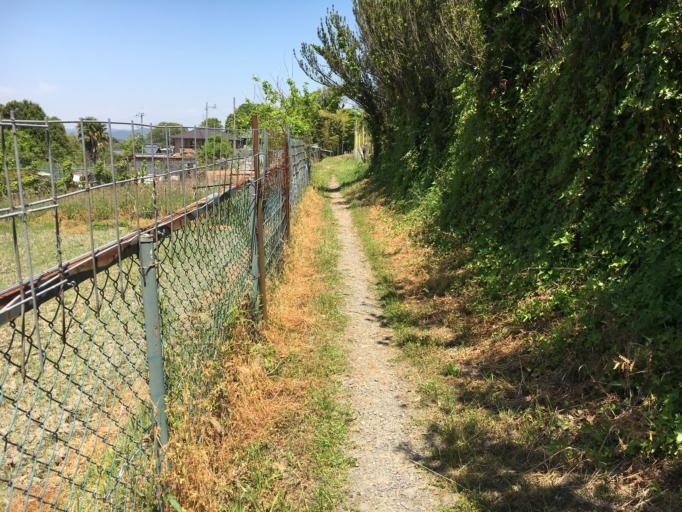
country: JP
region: Kyoto
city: Kameoka
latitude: 35.0274
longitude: 135.5910
